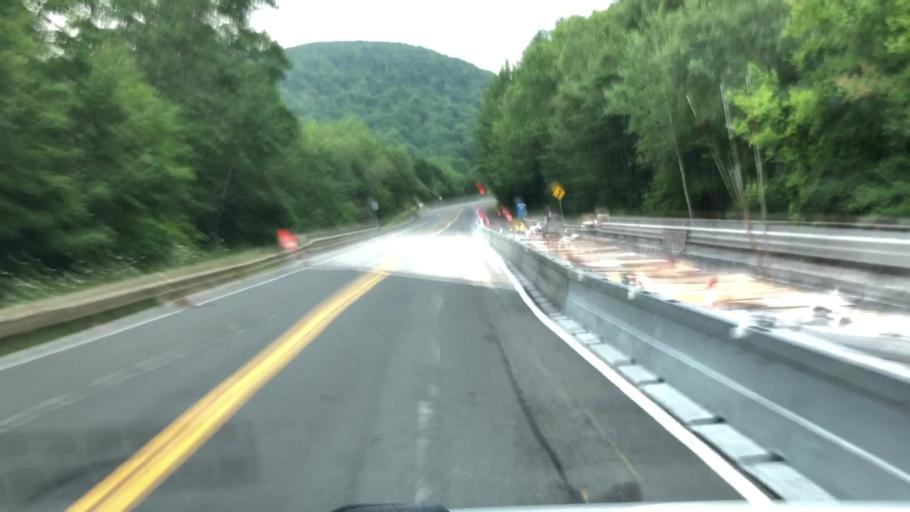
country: US
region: Massachusetts
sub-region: Berkshire County
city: Hinsdale
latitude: 42.4908
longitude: -72.9756
